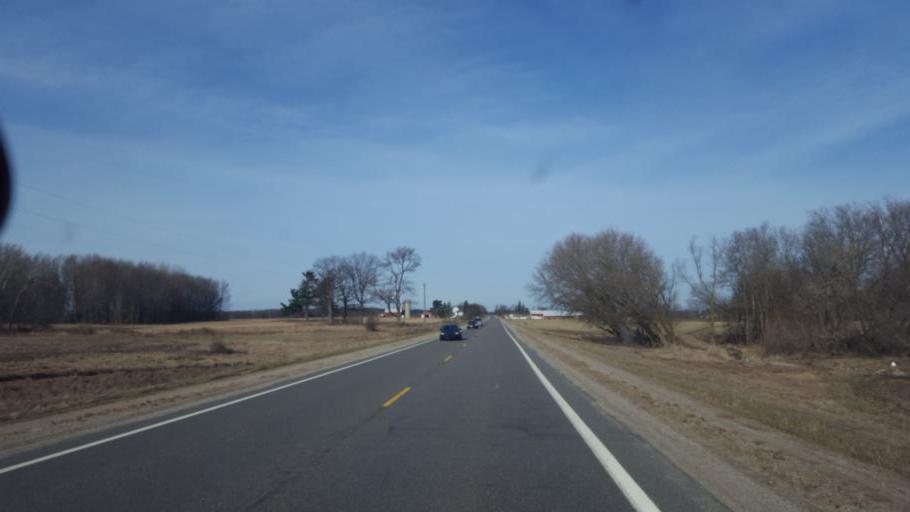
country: US
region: Michigan
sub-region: Montcalm County
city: Lakeview
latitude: 43.4314
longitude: -85.2963
